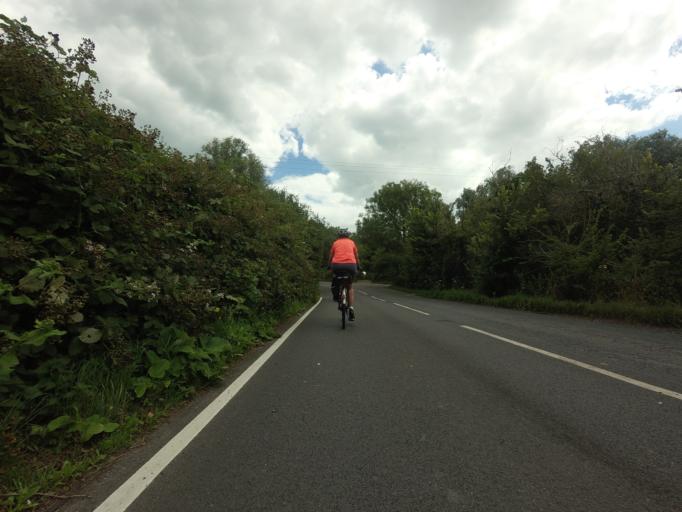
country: GB
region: England
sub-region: East Sussex
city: Pevensey
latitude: 50.8234
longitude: 0.3412
